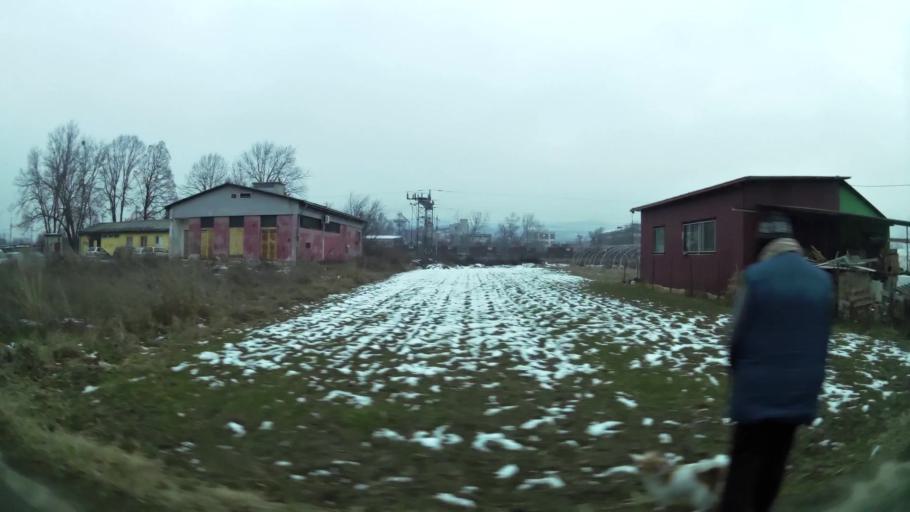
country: MK
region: Kisela Voda
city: Usje
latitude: 41.9680
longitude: 21.4788
